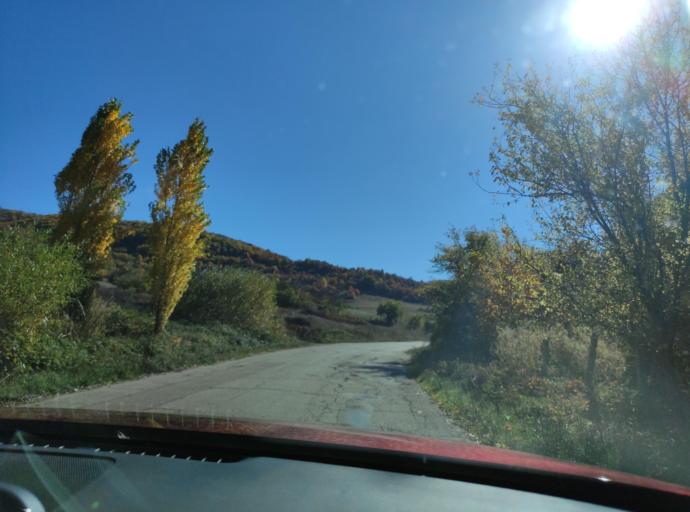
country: BG
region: Montana
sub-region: Obshtina Chiprovtsi
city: Chiprovtsi
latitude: 43.3881
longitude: 22.9222
